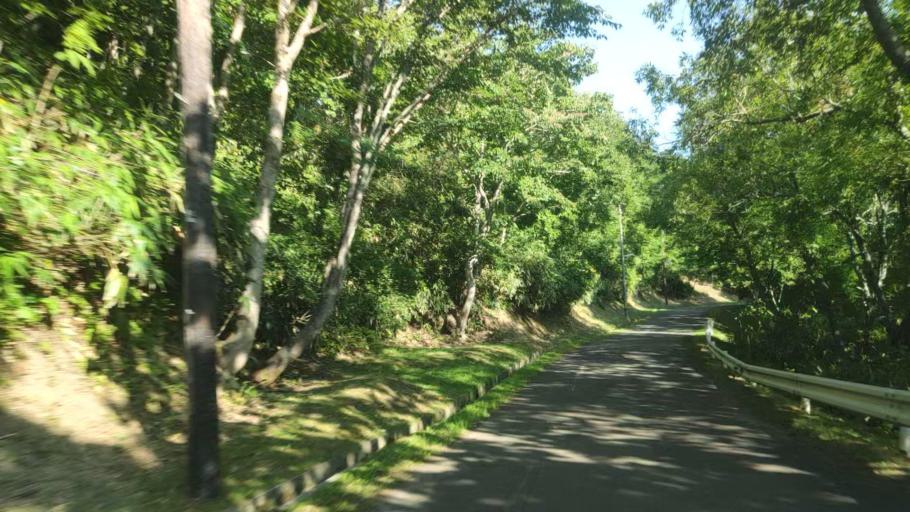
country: JP
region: Hokkaido
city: Wakkanai
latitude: 45.4146
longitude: 141.6676
